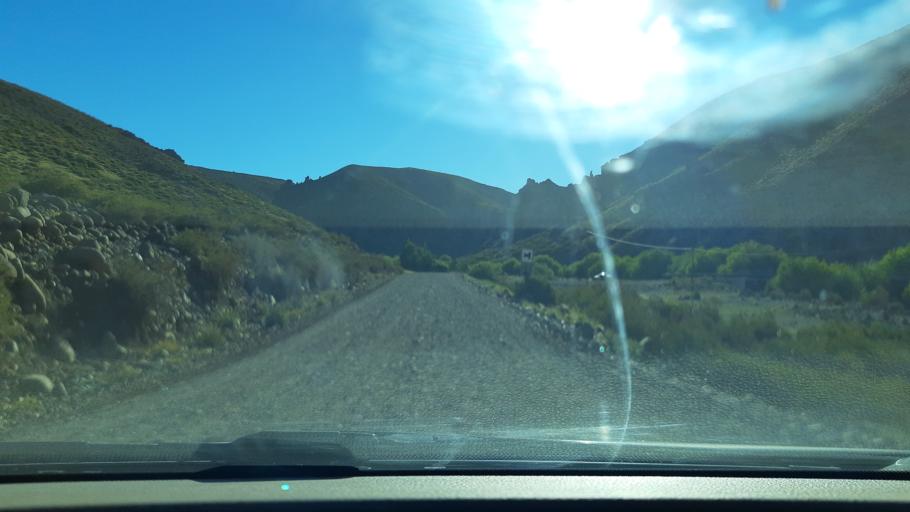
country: AR
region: Neuquen
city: Las Ovejas
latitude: -36.8019
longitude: -70.7281
